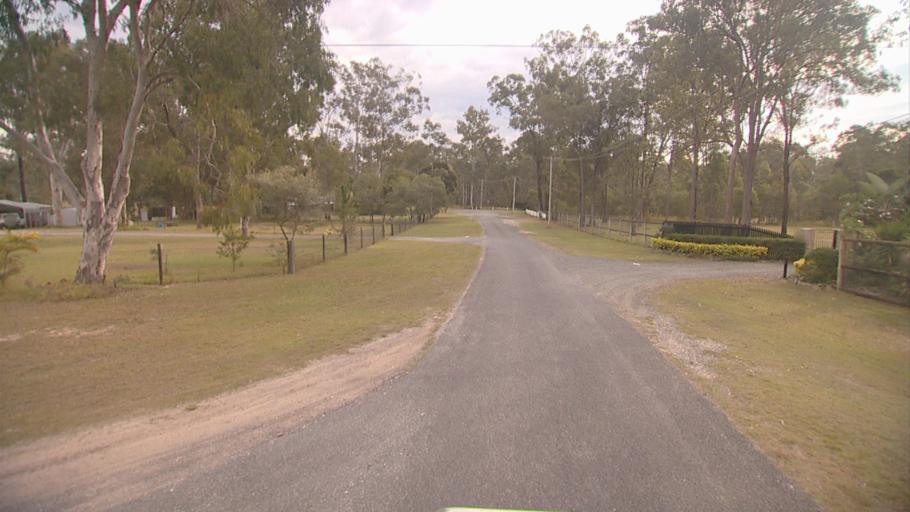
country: AU
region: Queensland
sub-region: Logan
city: Chambers Flat
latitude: -27.7750
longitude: 153.1138
